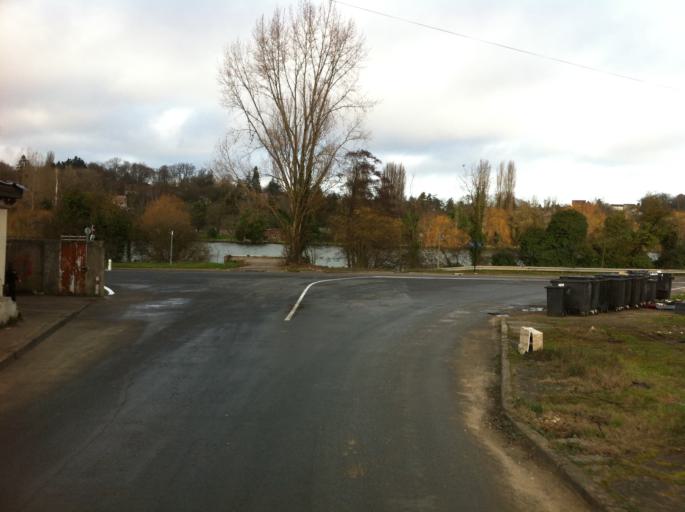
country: FR
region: Ile-de-France
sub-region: Departement de Seine-et-Marne
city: Le Mee-sur-Seine
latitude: 48.5275
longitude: 2.6370
